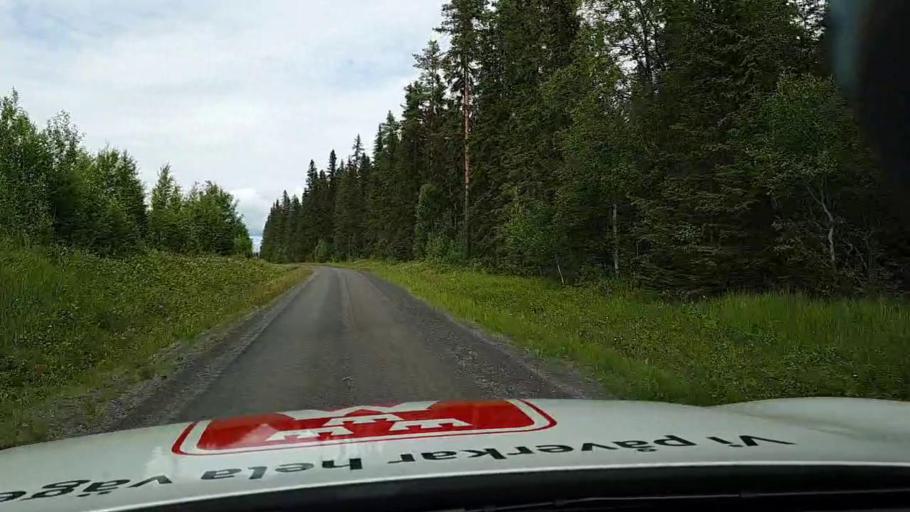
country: SE
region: Jaemtland
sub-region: OEstersunds Kommun
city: Lit
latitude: 63.2881
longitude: 15.2427
